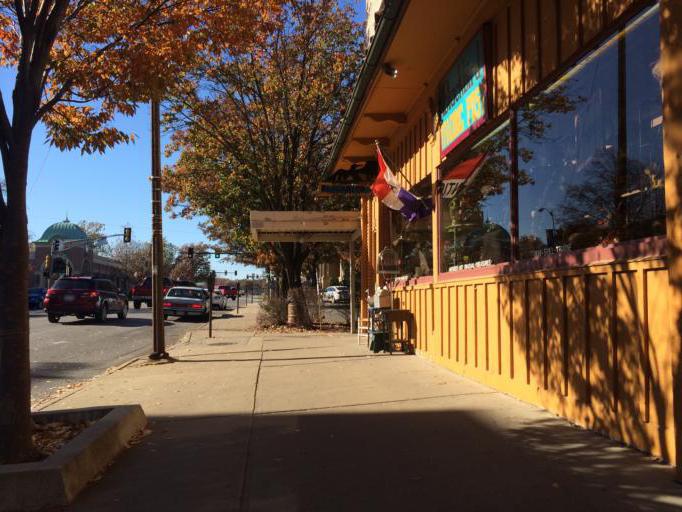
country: US
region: Kansas
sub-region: Douglas County
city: Lawrence
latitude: 38.9675
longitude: -95.2363
